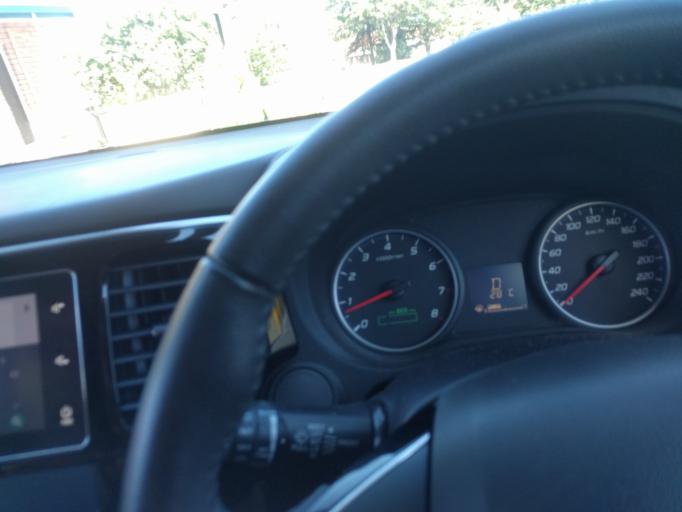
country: AU
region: New South Wales
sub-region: Armidale Dumaresq
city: Armidale
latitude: -30.4945
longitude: 151.6695
